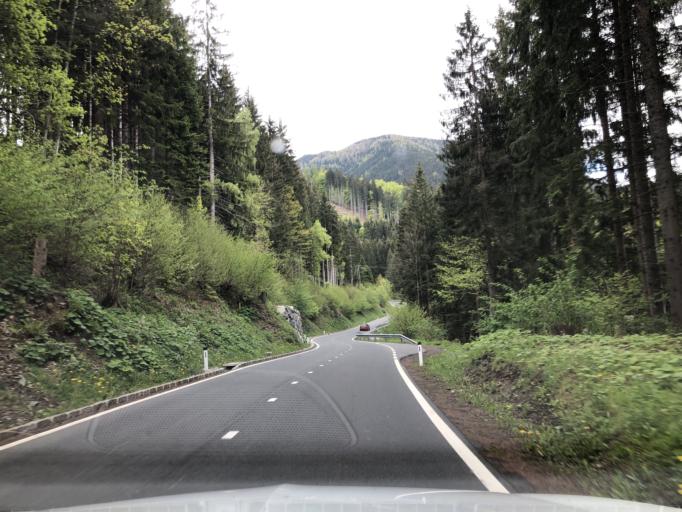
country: AT
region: Carinthia
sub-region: Politischer Bezirk Villach Land
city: Arnoldstein
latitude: 46.5319
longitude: 13.7495
